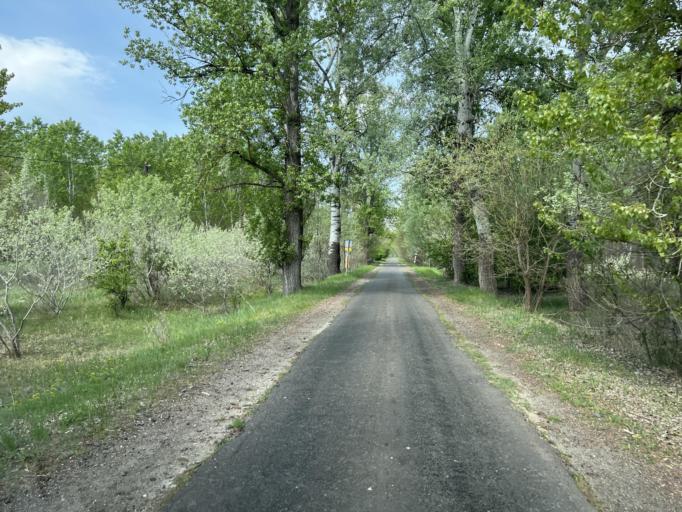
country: HU
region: Pest
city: Kocser
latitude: 47.0462
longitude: 19.9243
